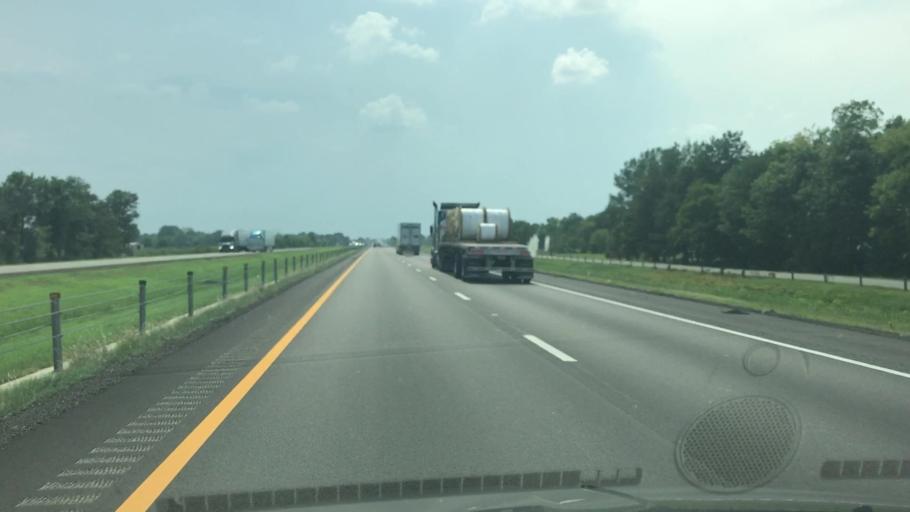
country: US
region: Arkansas
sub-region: Crittenden County
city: Earle
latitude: 35.1435
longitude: -90.4185
